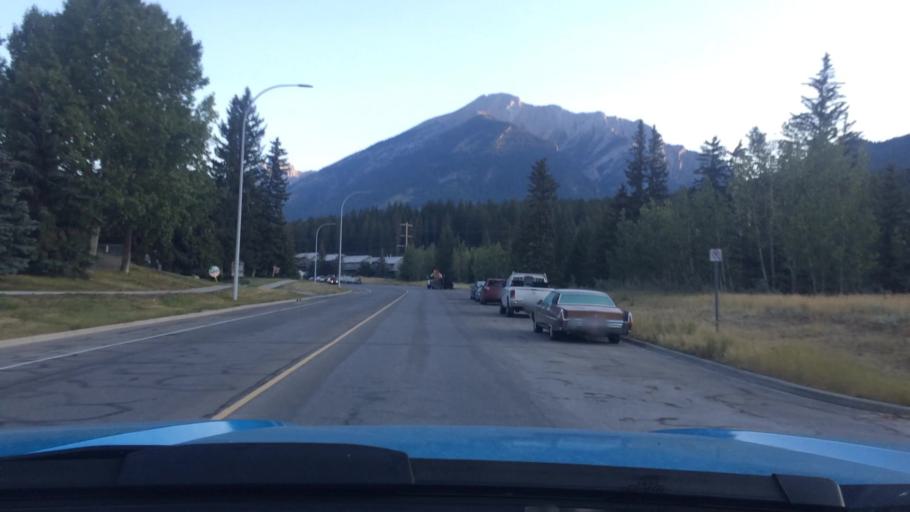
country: CA
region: Alberta
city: Canmore
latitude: 51.0793
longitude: -115.3212
